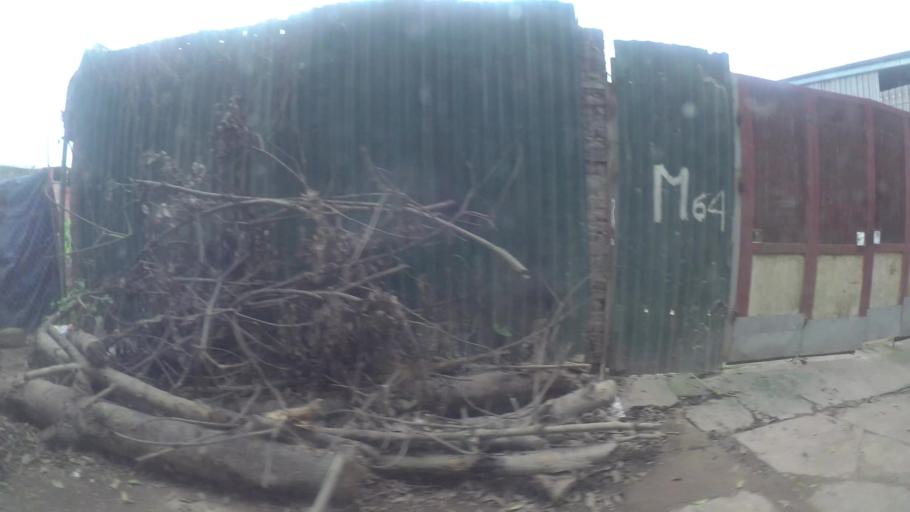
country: VN
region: Ha Noi
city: Tay Ho
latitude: 21.0647
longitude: 105.8369
